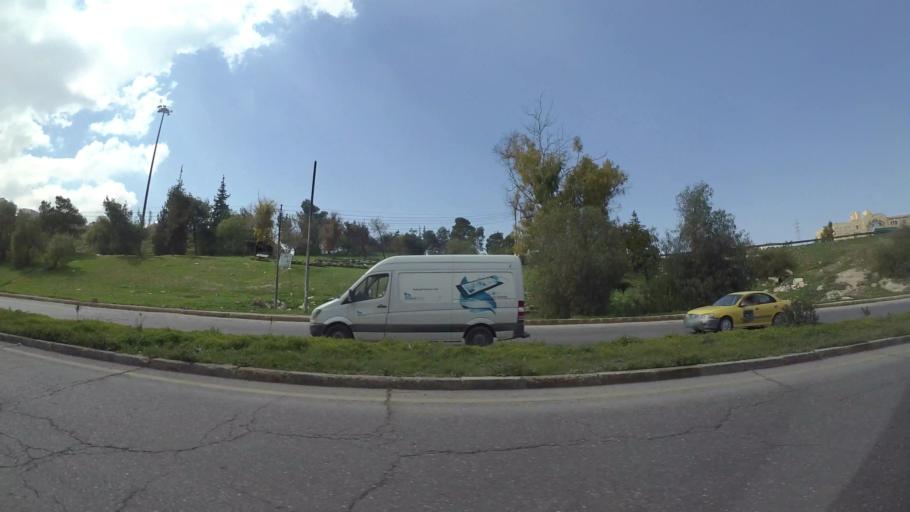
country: JO
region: Amman
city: Amman
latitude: 31.9889
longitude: 35.9776
